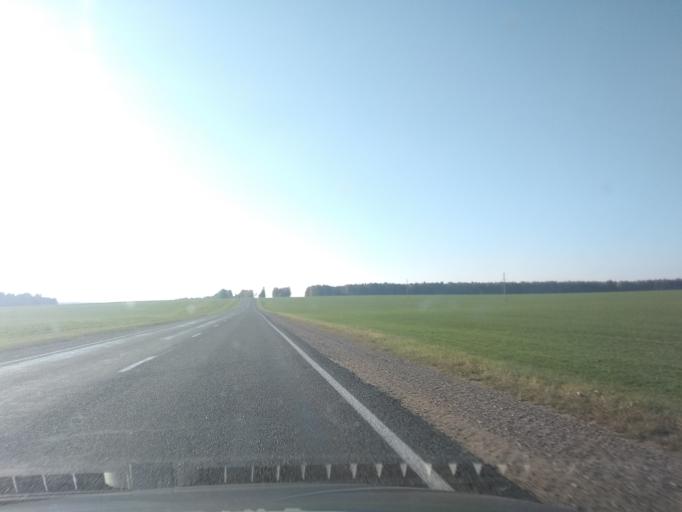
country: BY
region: Grodnenskaya
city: Svislach
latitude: 53.1293
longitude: 24.1535
